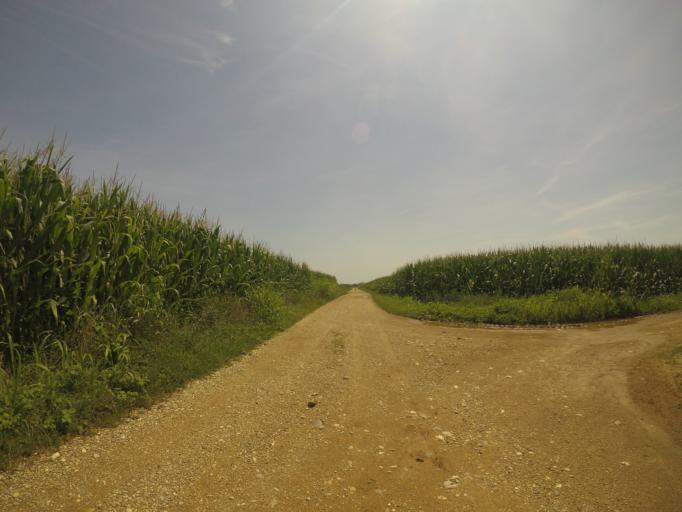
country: IT
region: Friuli Venezia Giulia
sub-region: Provincia di Udine
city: Lestizza
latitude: 45.9698
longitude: 13.0967
